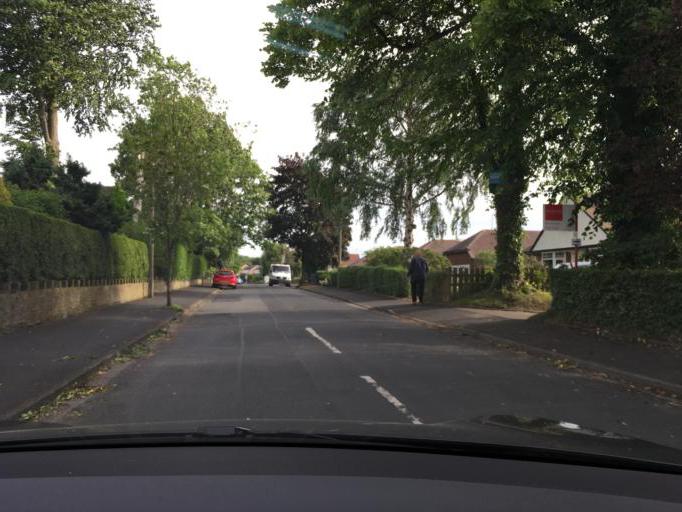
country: GB
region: England
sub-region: Borough of Stockport
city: Hazel Grove
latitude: 53.3793
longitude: -2.1052
